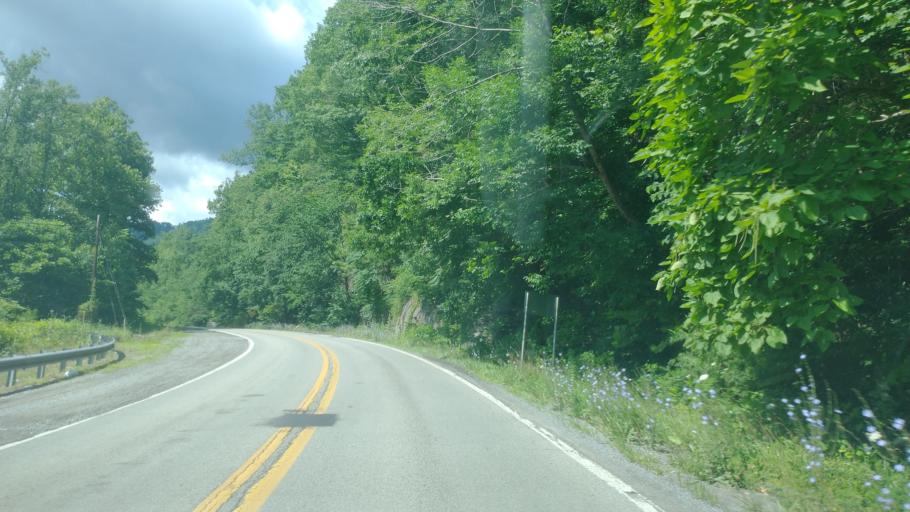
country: US
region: West Virginia
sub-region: McDowell County
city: Welch
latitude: 37.4205
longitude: -81.5178
